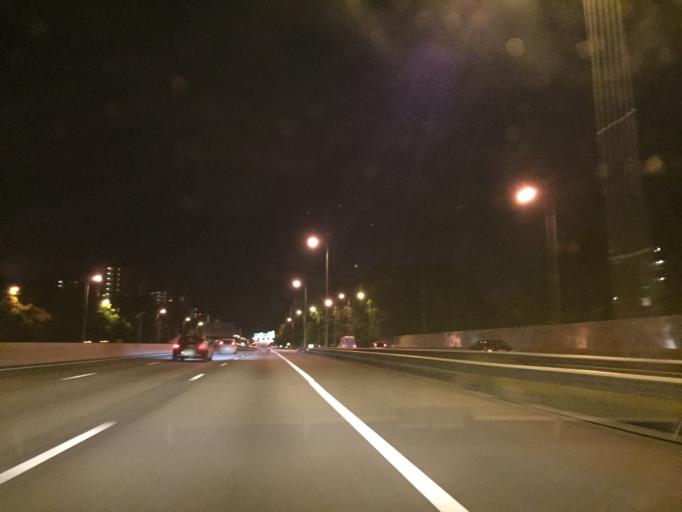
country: NL
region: North Holland
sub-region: Gemeente Amsterdam
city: Amsterdam
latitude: 52.3699
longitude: 4.8420
